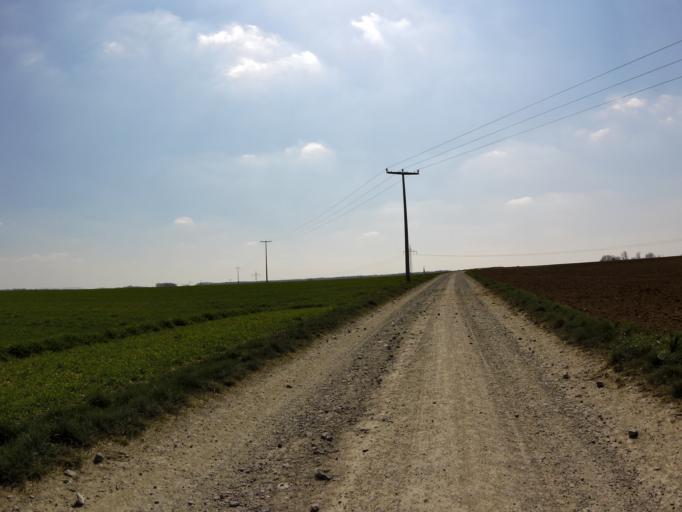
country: DE
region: Bavaria
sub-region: Regierungsbezirk Unterfranken
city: Biebelried
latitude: 49.7404
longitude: 10.0881
